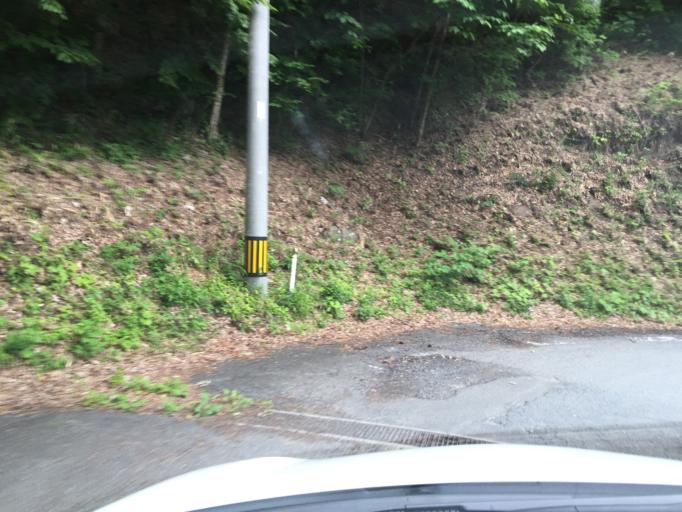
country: JP
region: Fukushima
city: Iwaki
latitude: 37.2091
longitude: 140.7225
